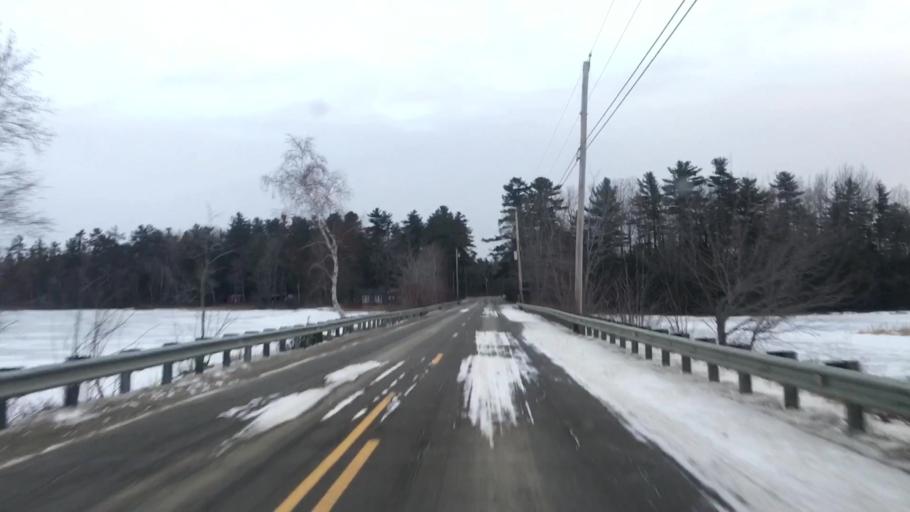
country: US
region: Maine
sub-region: Hancock County
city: Ellsworth
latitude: 44.6146
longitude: -68.3865
